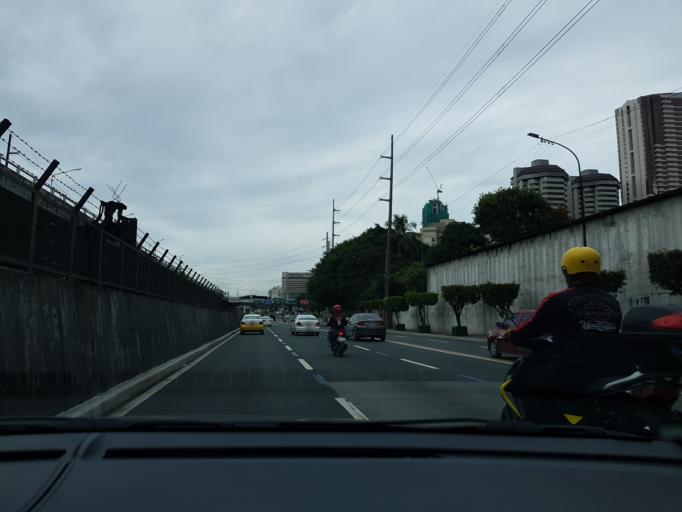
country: PH
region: Metro Manila
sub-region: Makati City
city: Makati City
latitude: 14.5524
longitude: 121.0317
